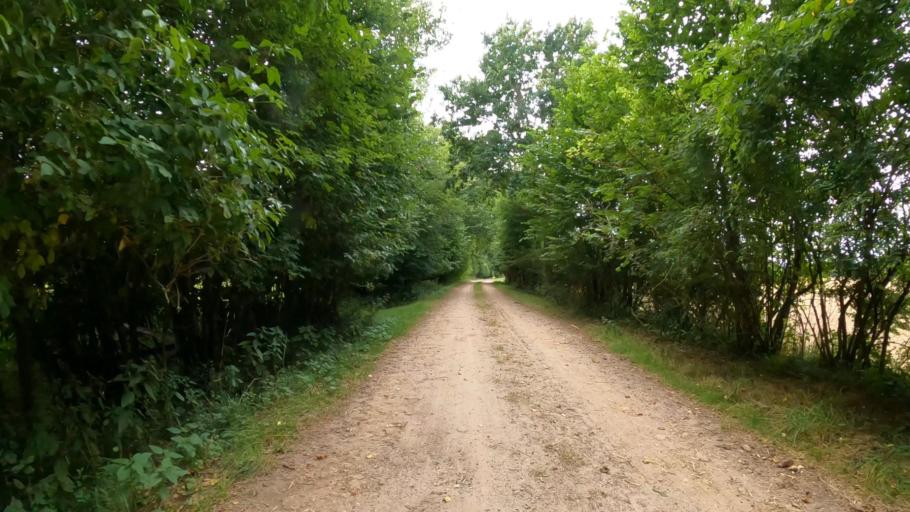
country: DE
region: Schleswig-Holstein
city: Fredesdorf
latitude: 53.8555
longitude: 10.2156
